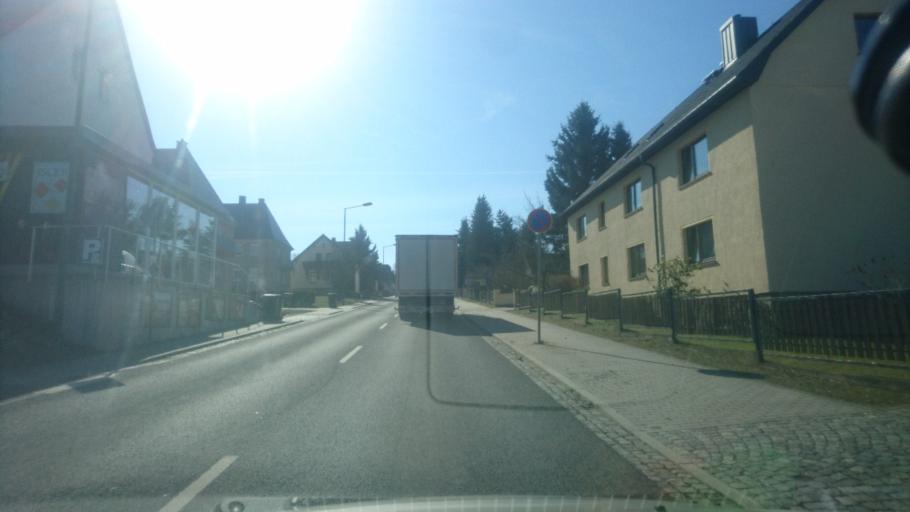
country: DE
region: Saxony
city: Auerbach
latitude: 50.5006
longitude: 12.4170
